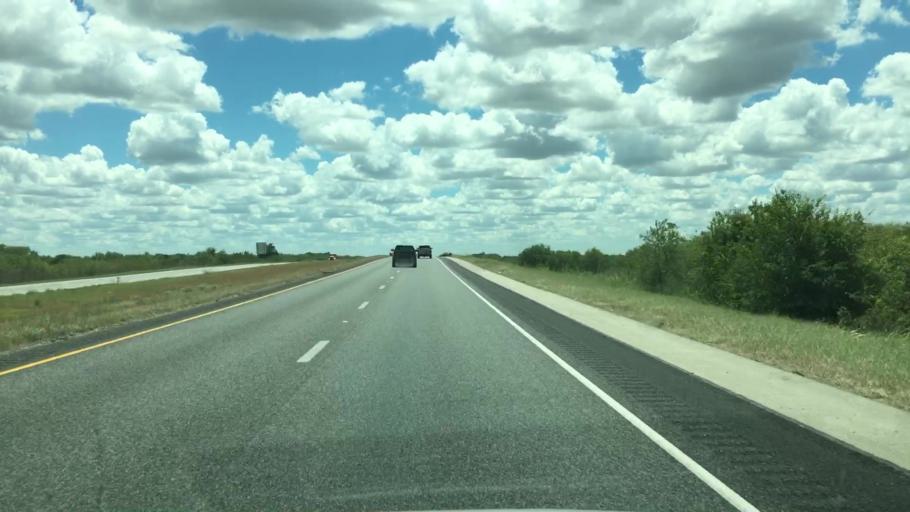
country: US
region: Texas
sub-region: Atascosa County
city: Pleasanton
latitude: 29.0896
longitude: -98.4331
